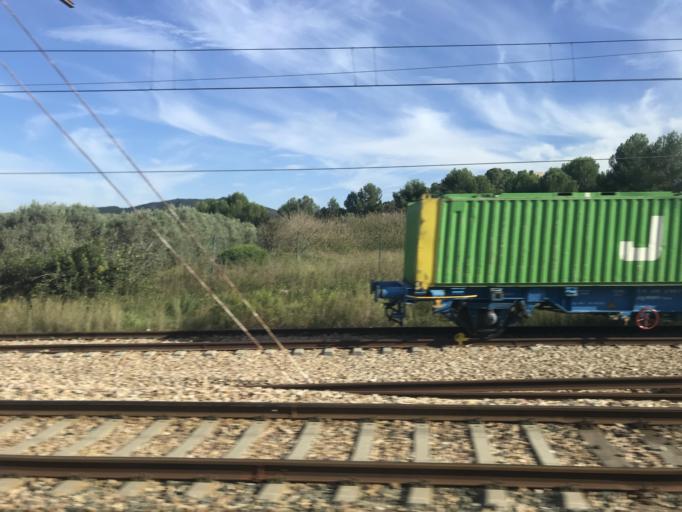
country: ES
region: Catalonia
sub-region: Provincia de Tarragona
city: Ulldecona
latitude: 40.5924
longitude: 0.4458
